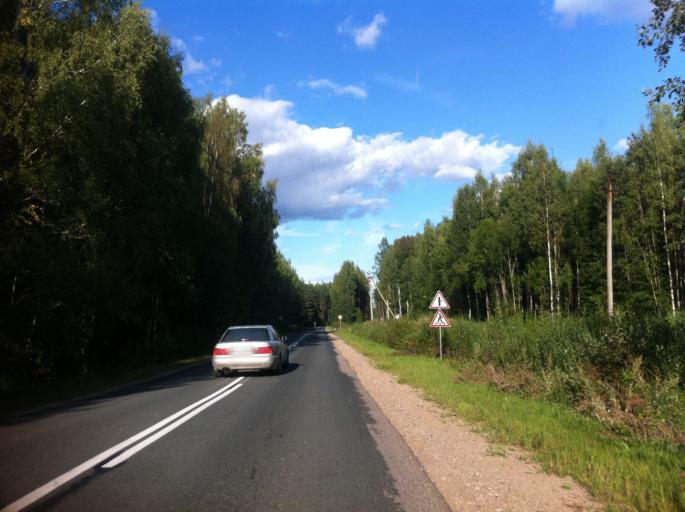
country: RU
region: Pskov
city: Izborsk
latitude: 57.8192
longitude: 27.8405
